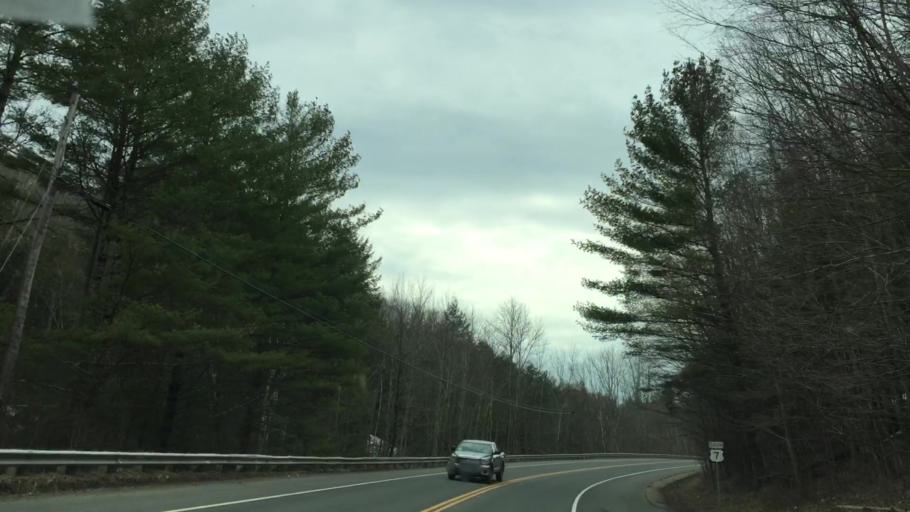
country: US
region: Massachusetts
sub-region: Berkshire County
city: Lanesborough
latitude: 42.6114
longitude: -73.2320
